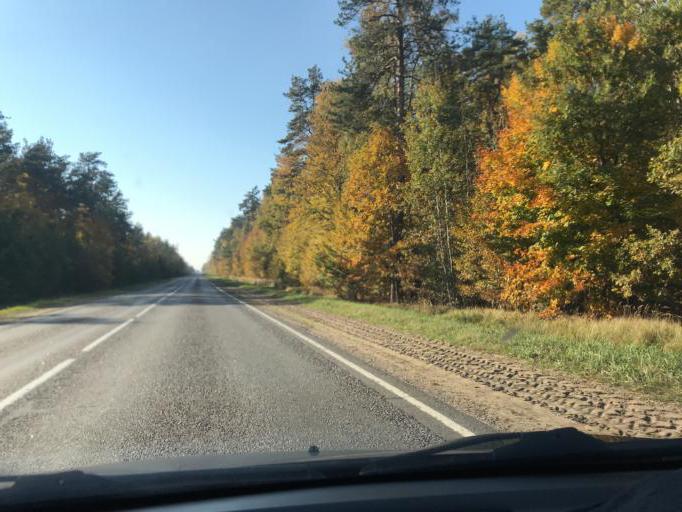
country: BY
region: Mogilev
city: Hlusha
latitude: 53.1031
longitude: 29.0397
